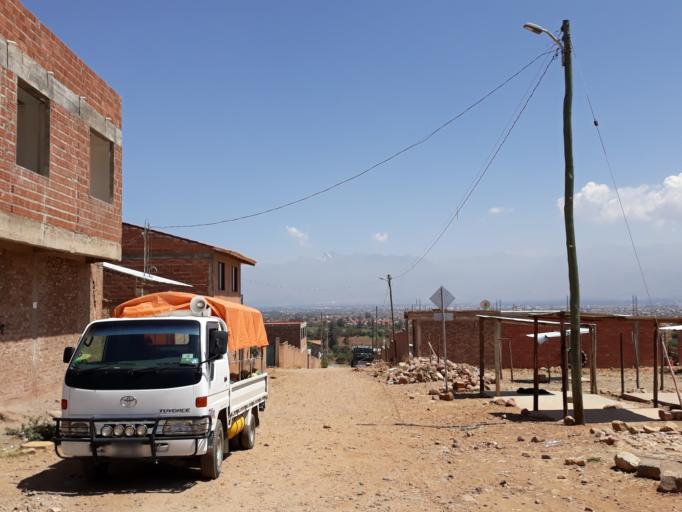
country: BO
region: Cochabamba
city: Cochabamba
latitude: -17.4634
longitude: -66.1358
